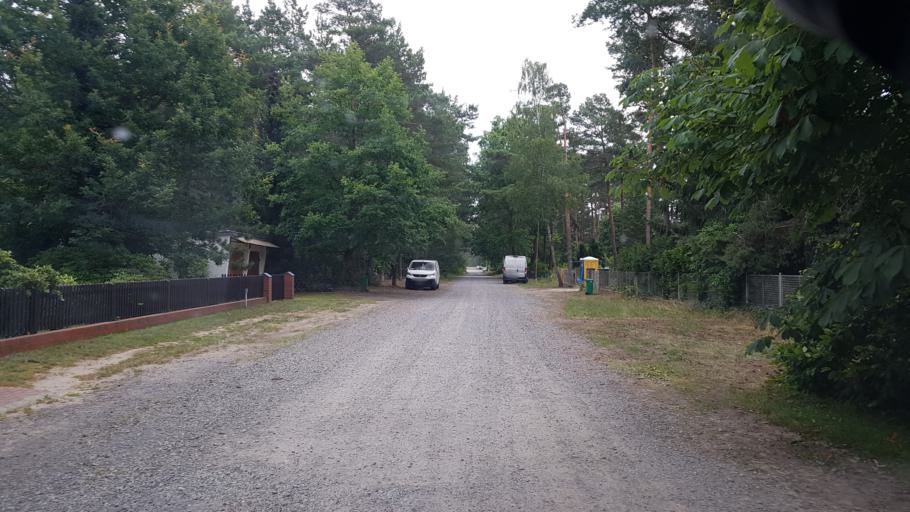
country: DE
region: Brandenburg
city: Gross Koris
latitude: 52.1634
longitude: 13.6960
